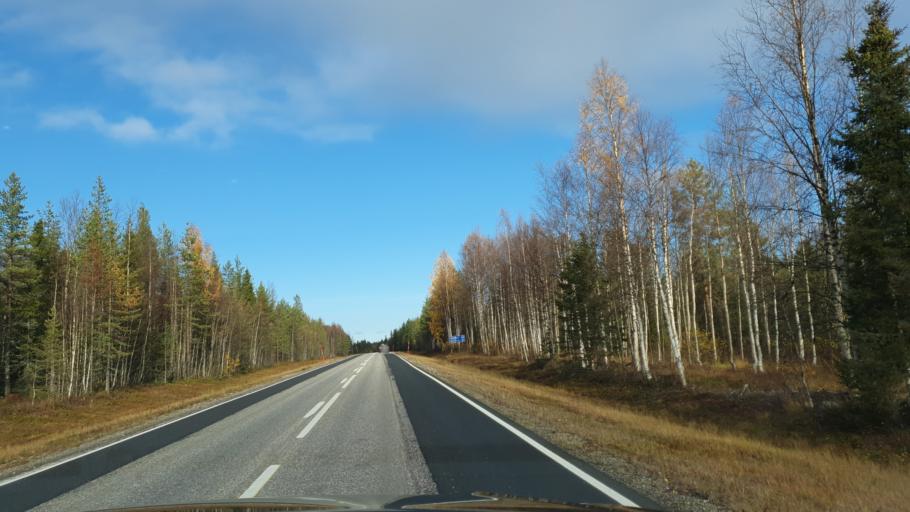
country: FI
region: Lapland
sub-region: Tunturi-Lappi
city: Kittilae
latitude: 67.2084
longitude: 24.9298
